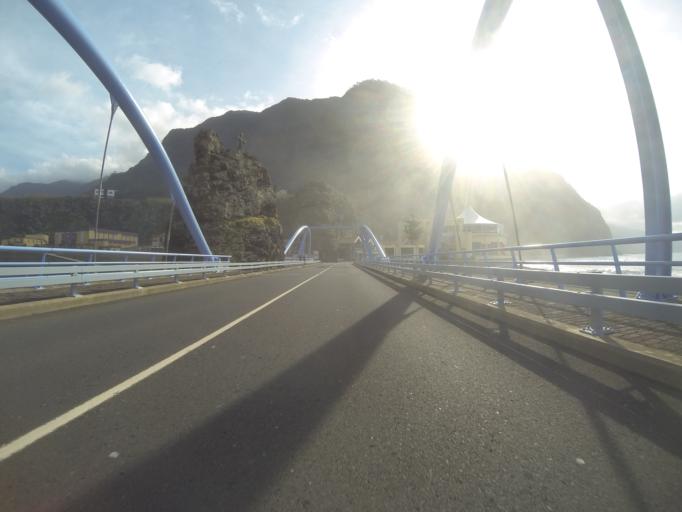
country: PT
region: Madeira
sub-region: Sao Vicente
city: Sao Vicente
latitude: 32.8084
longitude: -17.0482
